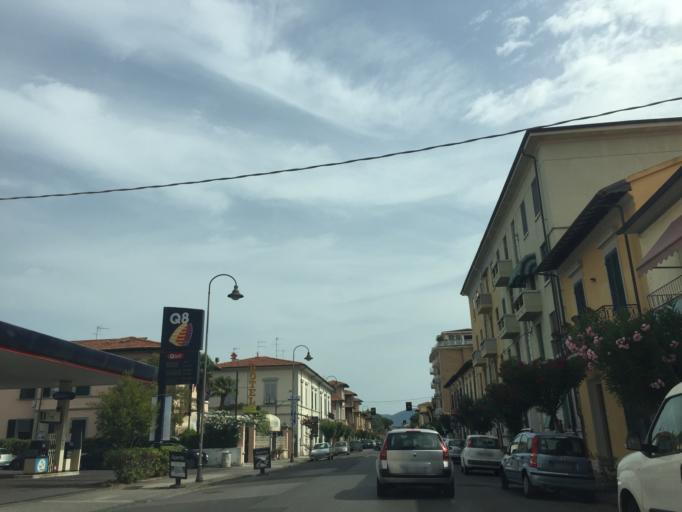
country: IT
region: Tuscany
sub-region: Province of Pisa
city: Pisa
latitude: 43.7173
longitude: 10.3889
